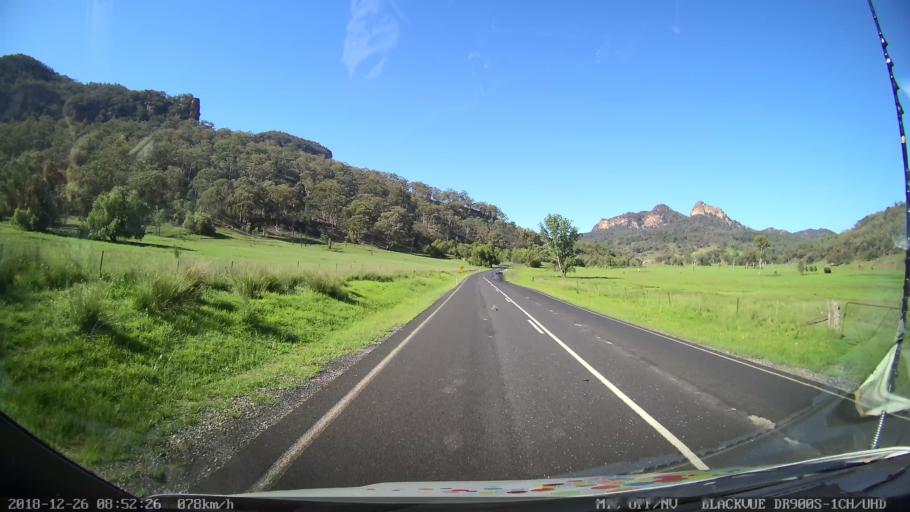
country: AU
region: New South Wales
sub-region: Mid-Western Regional
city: Kandos
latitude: -32.5967
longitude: 150.0861
